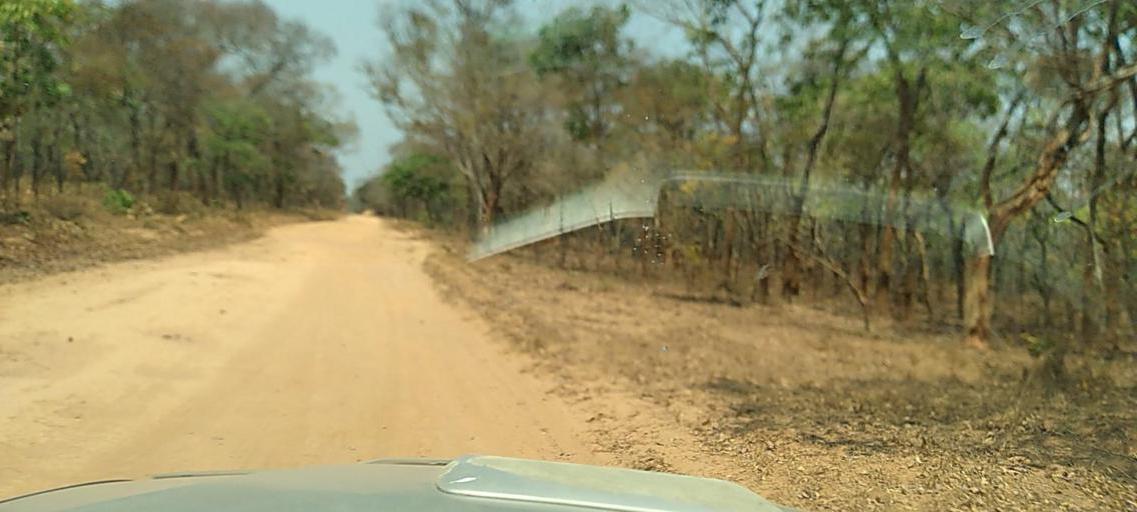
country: ZM
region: North-Western
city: Kasempa
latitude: -13.6623
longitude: 26.2742
